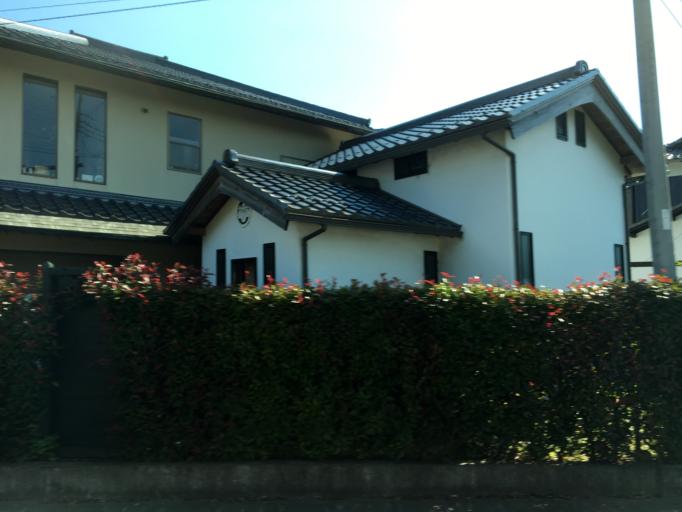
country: JP
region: Saitama
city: Sakado
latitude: 35.9618
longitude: 139.3643
